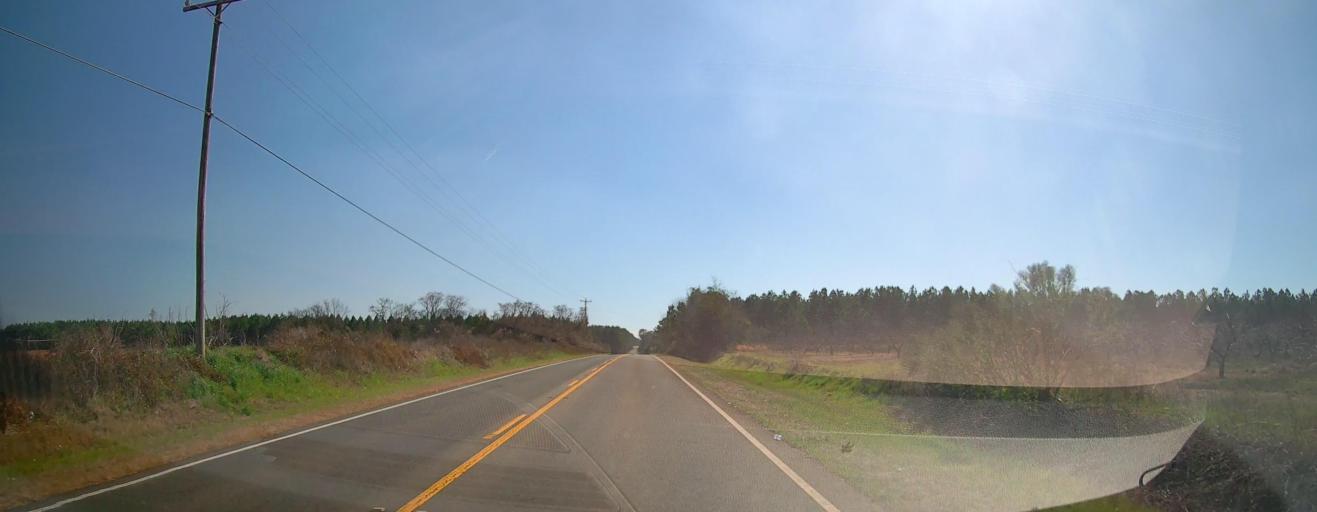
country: US
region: Georgia
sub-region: Macon County
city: Montezuma
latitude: 32.3278
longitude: -84.0221
